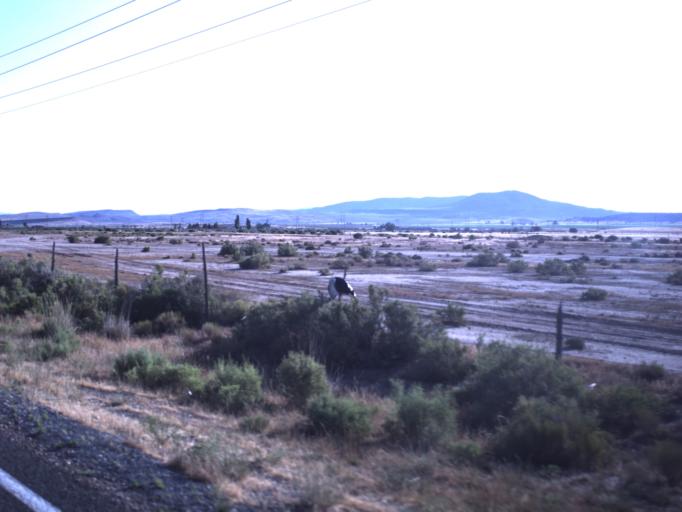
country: US
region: Utah
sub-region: Iron County
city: Enoch
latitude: 37.7896
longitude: -113.0507
